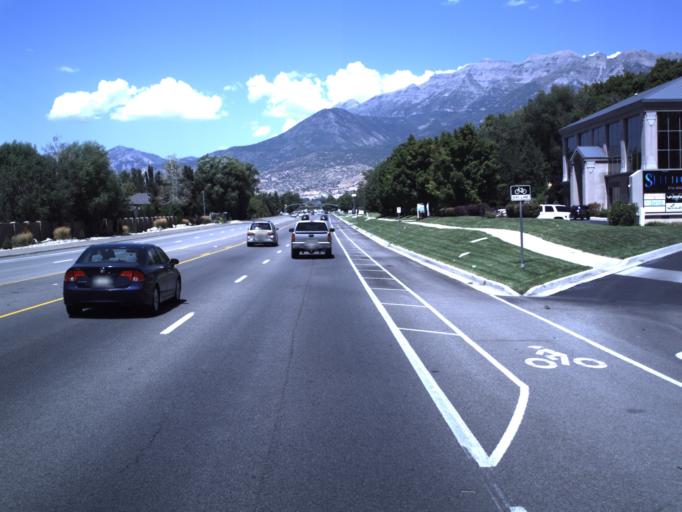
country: US
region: Utah
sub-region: Utah County
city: Provo
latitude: 40.2727
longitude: -111.6571
